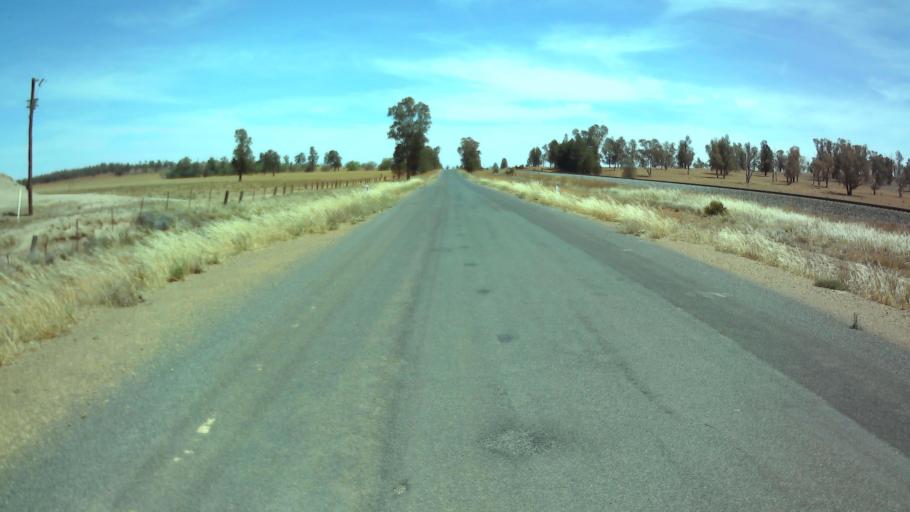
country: AU
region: New South Wales
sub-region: Weddin
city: Grenfell
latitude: -33.7683
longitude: 147.7580
